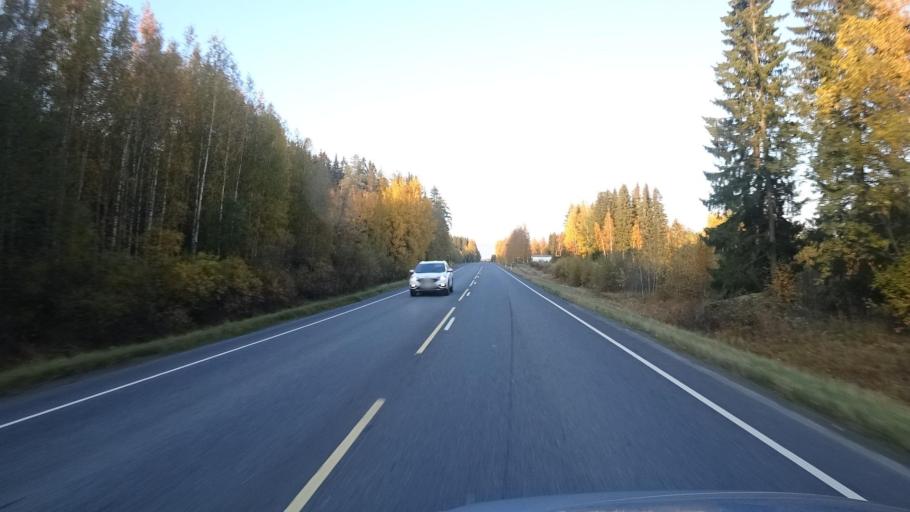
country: FI
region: Haeme
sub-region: Forssa
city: Jokioinen
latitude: 60.7927
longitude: 23.5015
